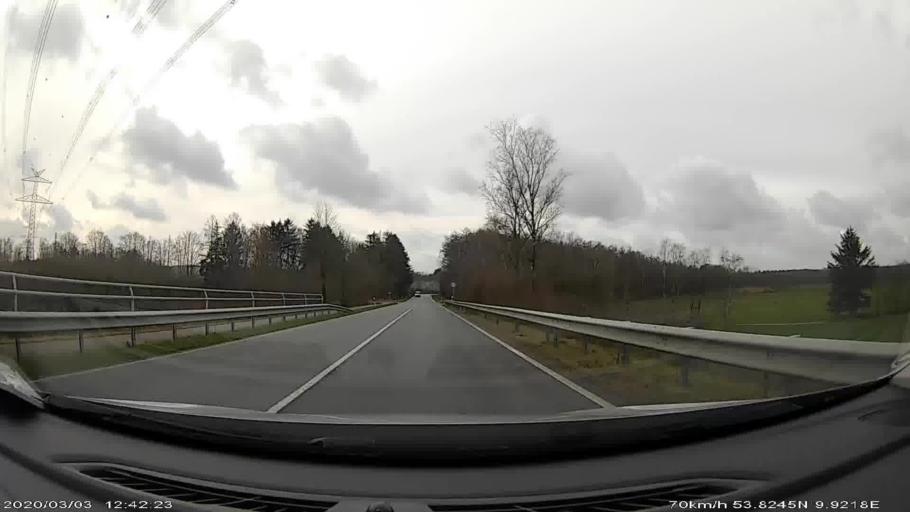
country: DE
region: Schleswig-Holstein
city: Kaltenkirchen
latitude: 53.8234
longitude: 9.9197
